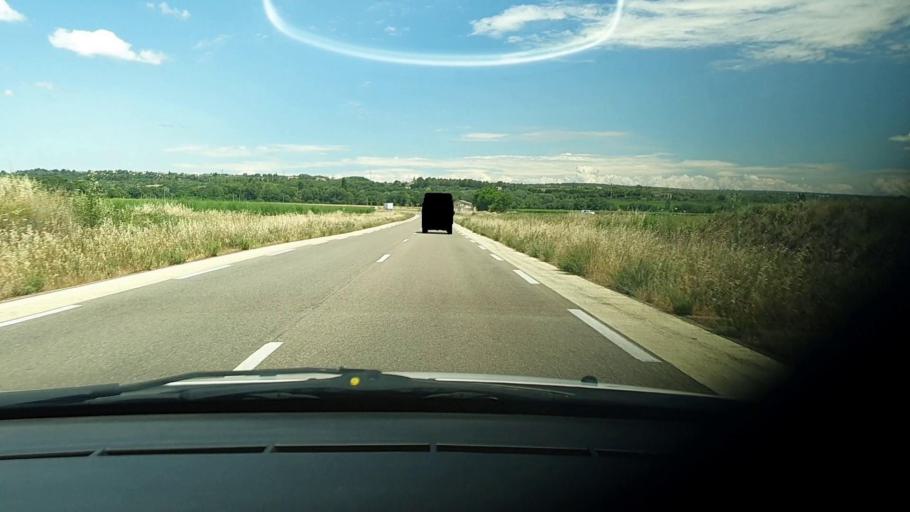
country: FR
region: Languedoc-Roussillon
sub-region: Departement du Gard
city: Uzes
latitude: 43.9925
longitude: 4.3895
